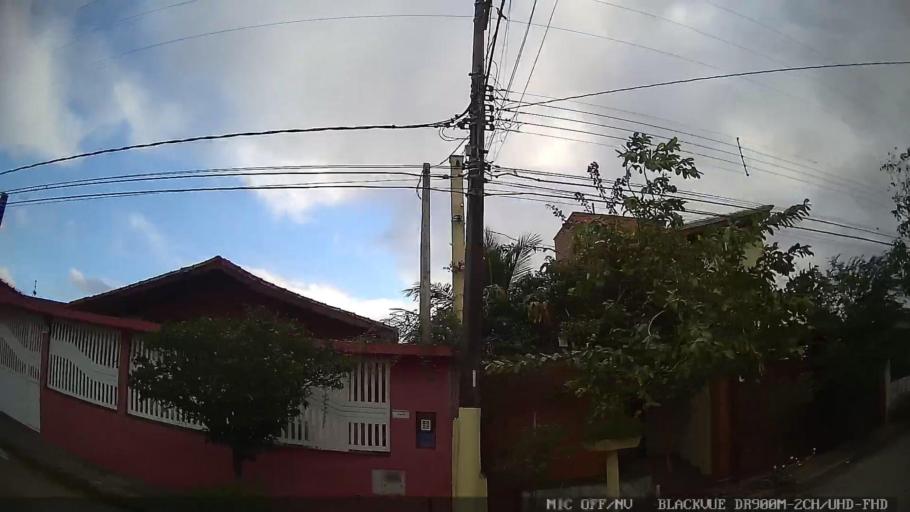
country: BR
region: Sao Paulo
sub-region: Peruibe
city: Peruibe
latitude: -24.3189
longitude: -46.9922
